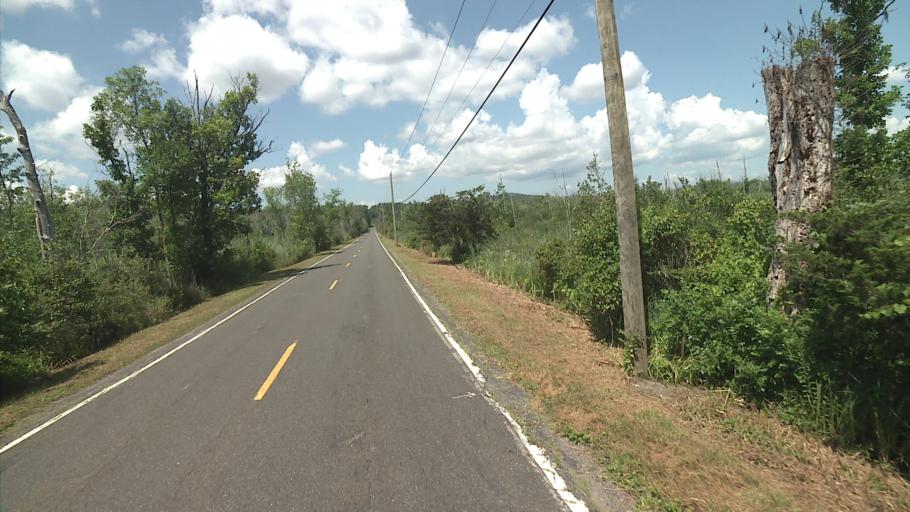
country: US
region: Connecticut
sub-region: Litchfield County
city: Canaan
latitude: 41.9501
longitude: -73.3376
